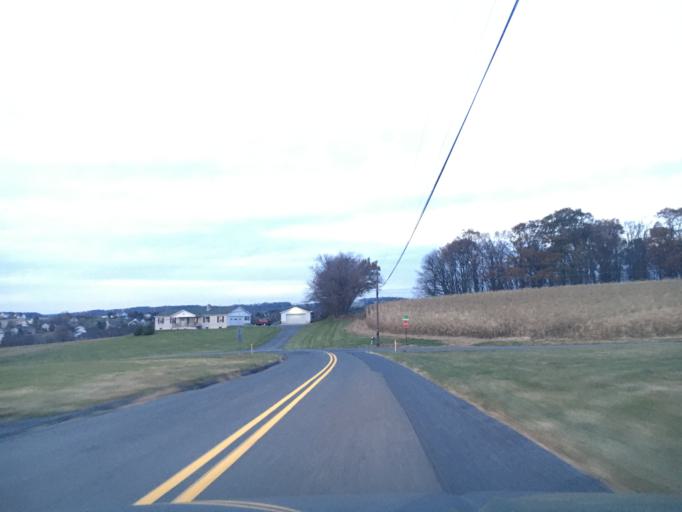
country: US
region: Pennsylvania
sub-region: Lehigh County
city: Schnecksville
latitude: 40.6948
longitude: -75.5794
